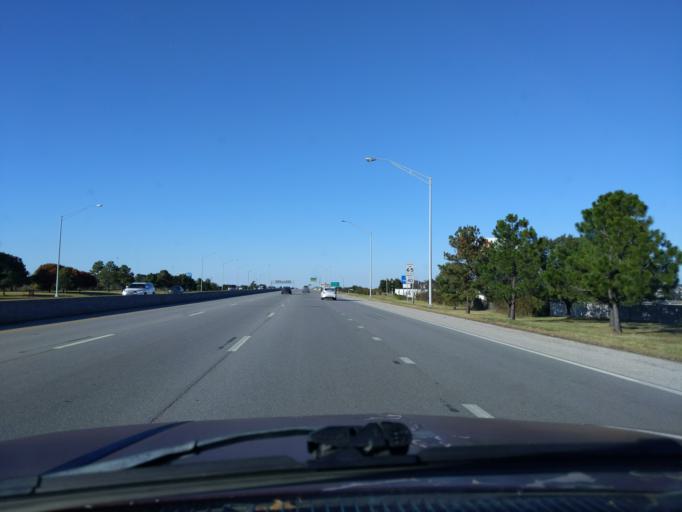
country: US
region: Oklahoma
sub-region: Tulsa County
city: Broken Arrow
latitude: 36.0407
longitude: -95.8589
